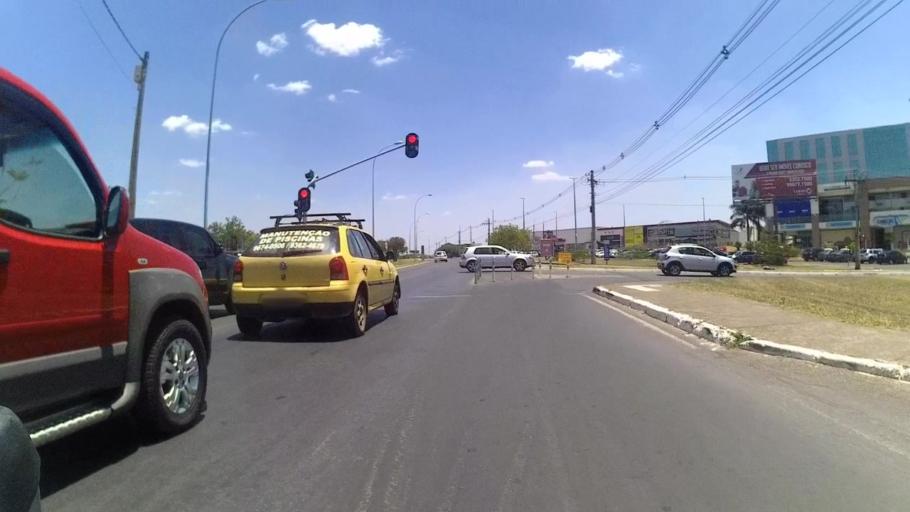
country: BR
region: Federal District
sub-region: Brasilia
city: Brasilia
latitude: -15.7224
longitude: -47.8812
